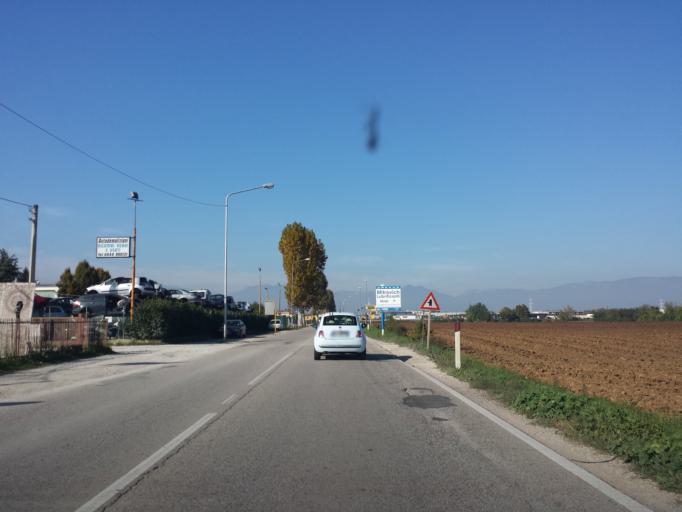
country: IT
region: Veneto
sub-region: Provincia di Vicenza
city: Crispi Cavour
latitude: 45.5804
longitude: 11.5078
